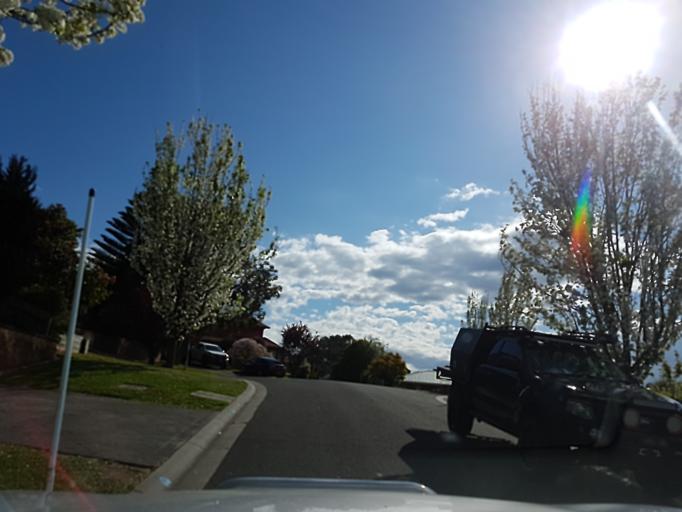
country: AU
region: Victoria
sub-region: Cardinia
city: Pakenham Upper
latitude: -38.0640
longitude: 145.4783
